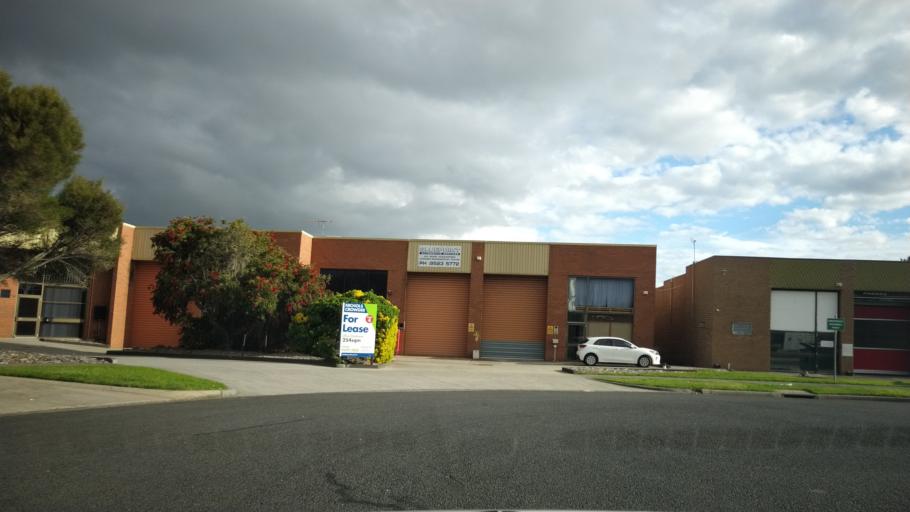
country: AU
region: Victoria
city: Highett
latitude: -37.9509
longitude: 145.0632
